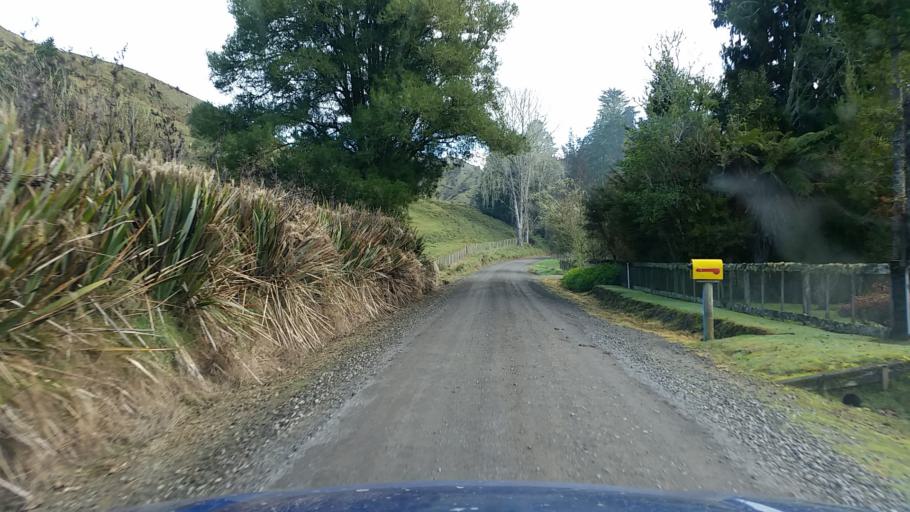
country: NZ
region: Taranaki
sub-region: New Plymouth District
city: Waitara
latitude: -39.1018
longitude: 174.8411
